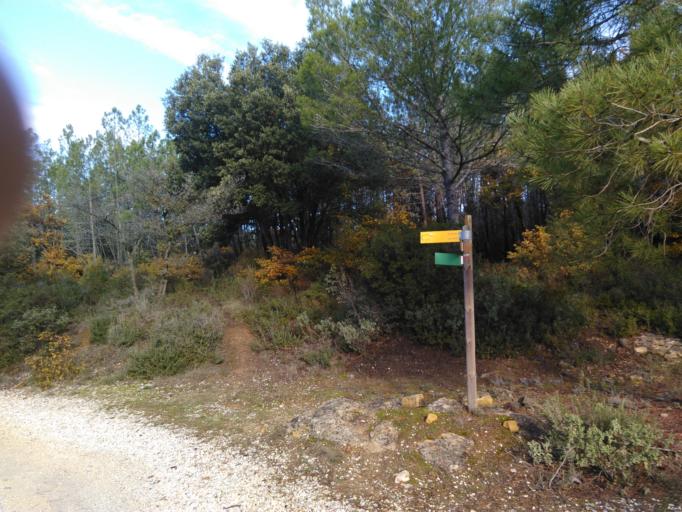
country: FR
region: Provence-Alpes-Cote d'Azur
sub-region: Departement du Vaucluse
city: Mornas
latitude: 44.2299
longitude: 4.7510
